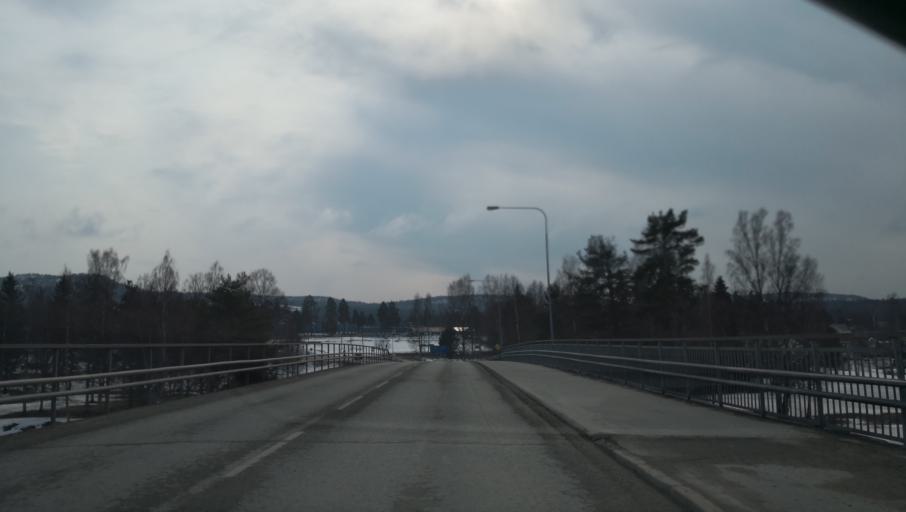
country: SE
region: Vaesternorrland
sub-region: OErnskoeldsviks Kommun
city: Ornskoldsvik
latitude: 63.2914
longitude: 18.6106
